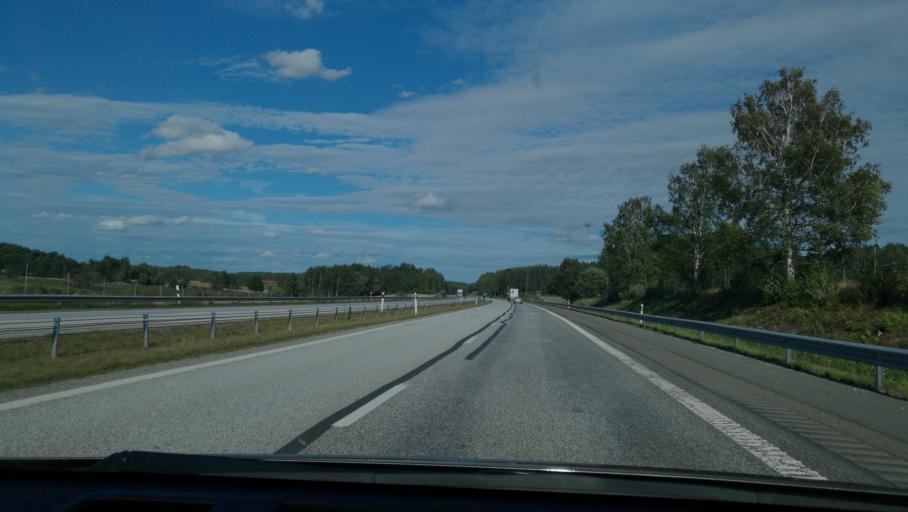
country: SE
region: OErebro
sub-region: Askersunds Kommun
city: Asbro
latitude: 59.0528
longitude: 14.9608
